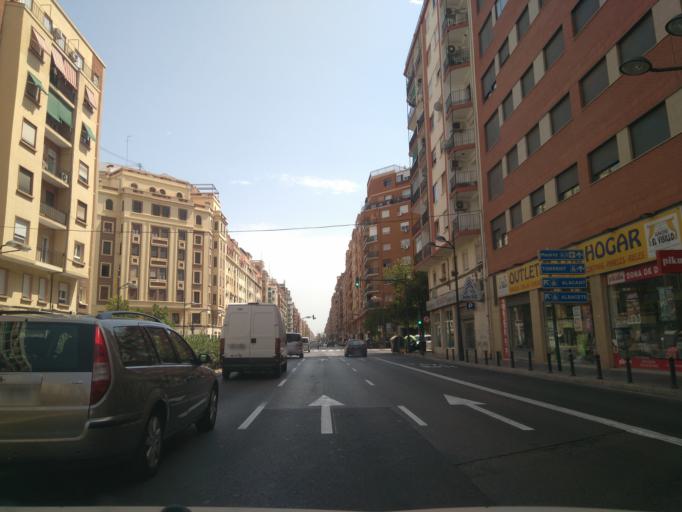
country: ES
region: Valencia
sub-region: Provincia de Valencia
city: Valencia
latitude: 39.4716
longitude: -0.3935
